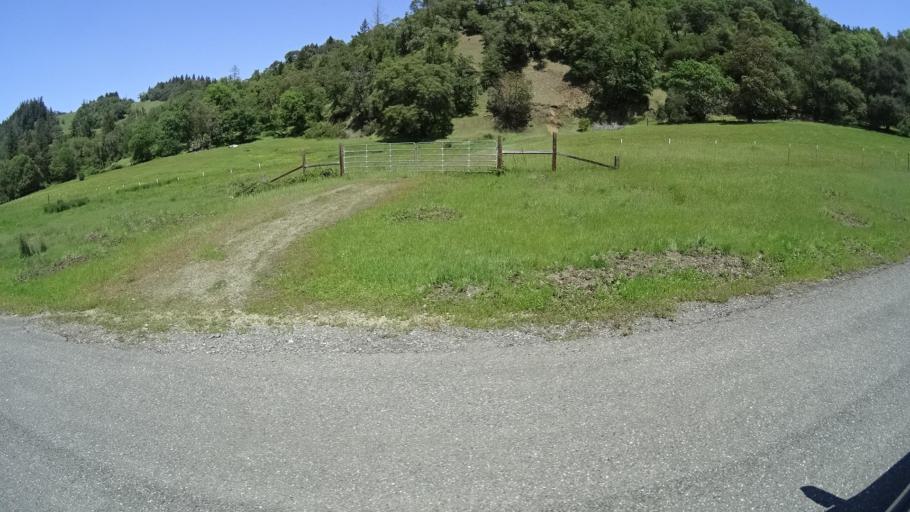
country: US
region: California
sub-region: Humboldt County
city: Redway
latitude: 40.2205
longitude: -123.6337
